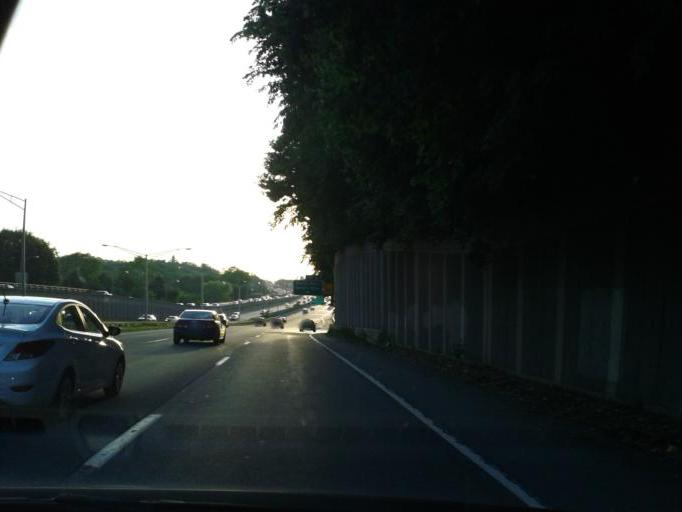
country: US
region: New York
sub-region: Westchester County
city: Bronxville
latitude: 40.9268
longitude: -73.8363
